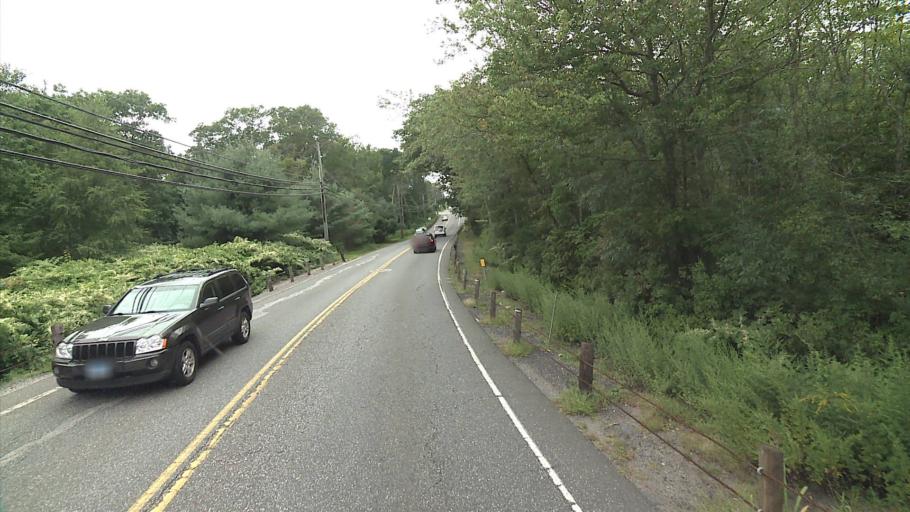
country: US
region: Connecticut
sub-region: New London County
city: Niantic
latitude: 41.3179
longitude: -72.2221
